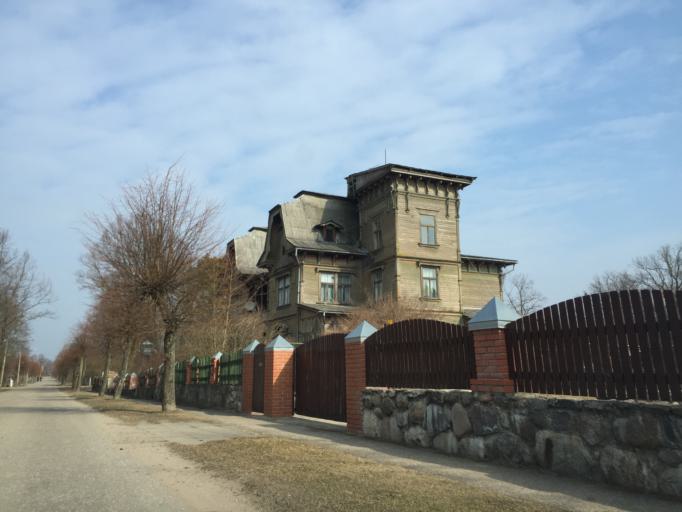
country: LV
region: Salacgrivas
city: Ainazi
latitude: 57.8648
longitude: 24.3589
